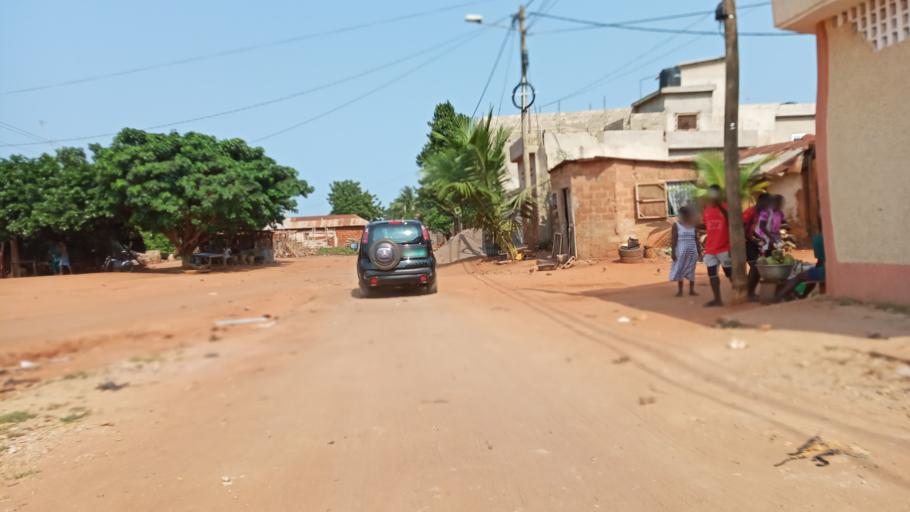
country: TG
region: Maritime
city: Lome
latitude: 6.2099
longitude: 1.1988
